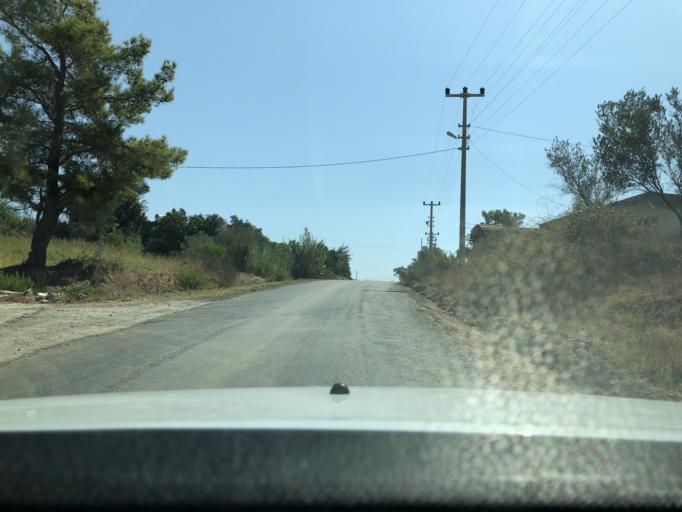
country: TR
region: Antalya
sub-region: Manavgat
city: Manavgat
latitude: 36.8219
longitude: 31.4997
